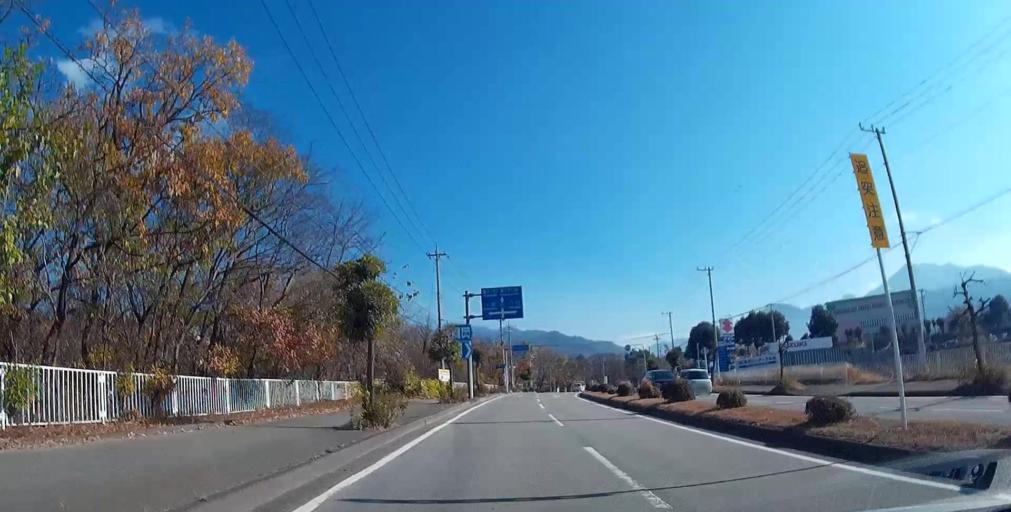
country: JP
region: Yamanashi
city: Isawa
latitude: 35.6317
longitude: 138.6799
